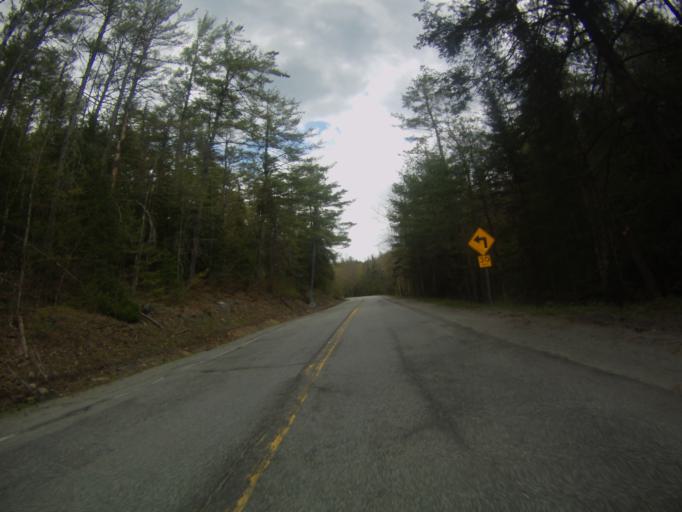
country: US
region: New York
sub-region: Essex County
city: Mineville
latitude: 44.0741
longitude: -73.6338
